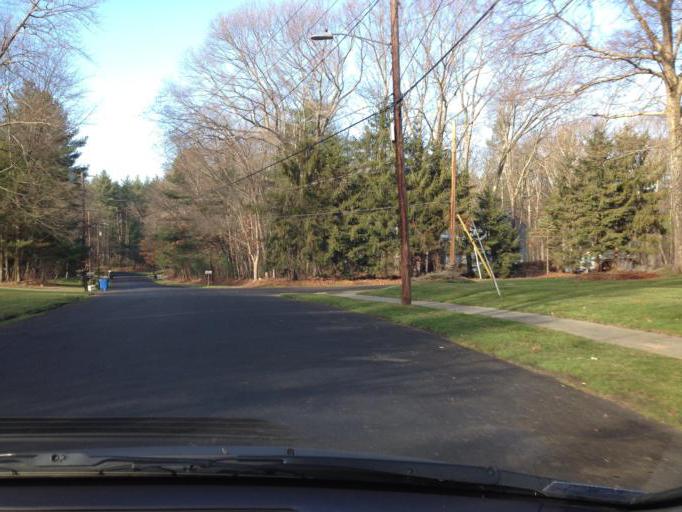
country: US
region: Massachusetts
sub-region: Middlesex County
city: Bedford
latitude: 42.5042
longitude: -71.2894
